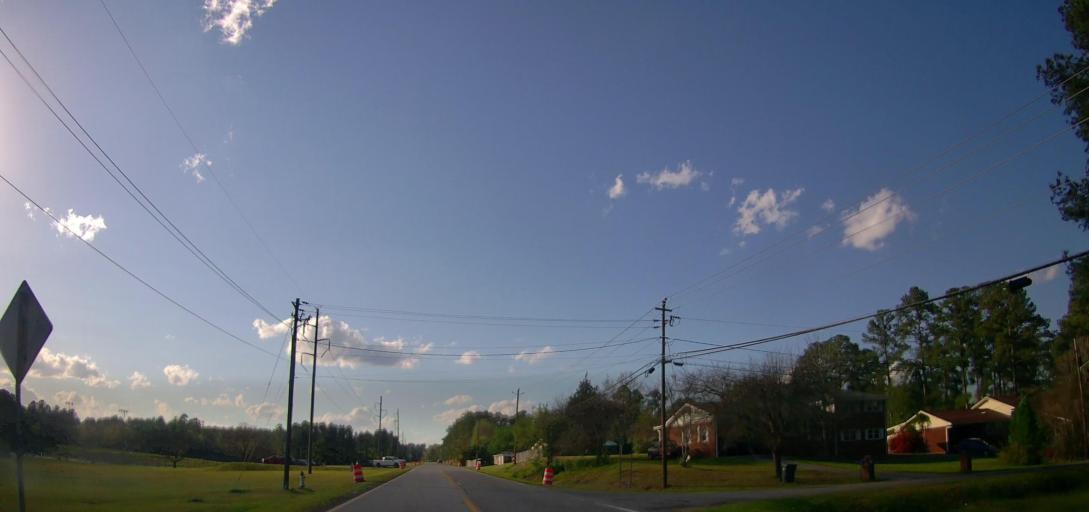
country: US
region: Georgia
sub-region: Baldwin County
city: Milledgeville
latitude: 33.0970
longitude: -83.2674
